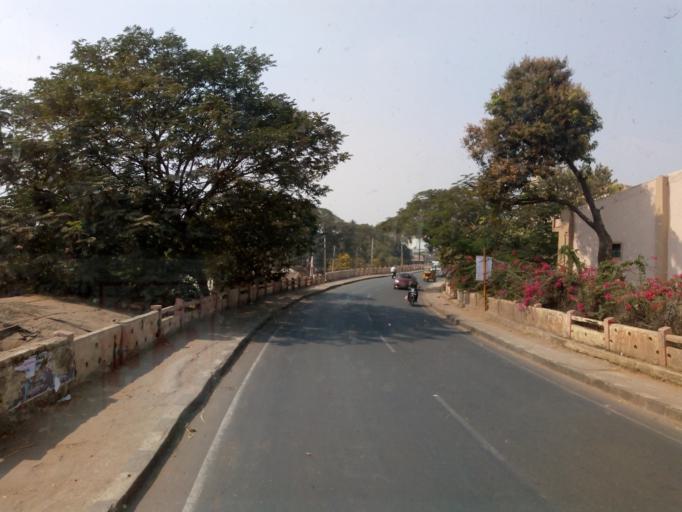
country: IN
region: Andhra Pradesh
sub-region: West Godavari
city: Eluru
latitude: 16.7084
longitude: 81.1004
